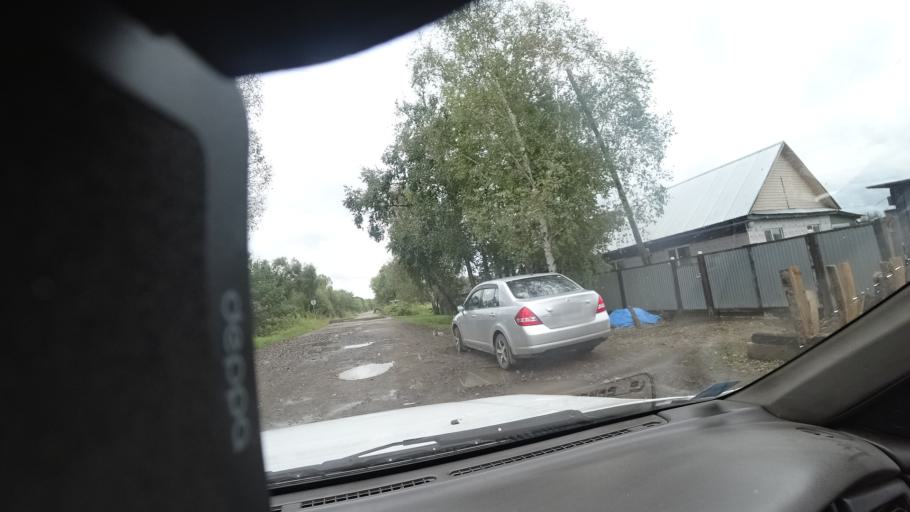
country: RU
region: Primorskiy
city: Dal'nerechensk
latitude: 45.9163
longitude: 133.7245
